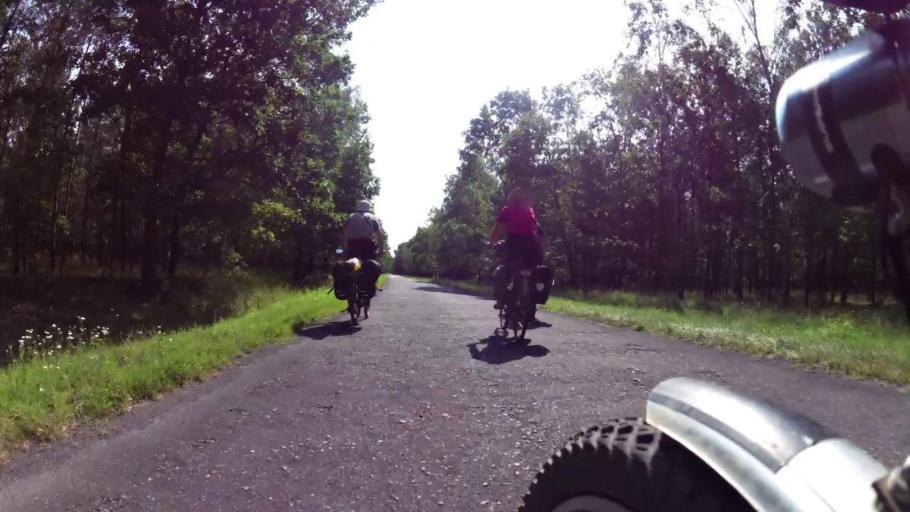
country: PL
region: West Pomeranian Voivodeship
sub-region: Powiat mysliborski
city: Boleszkowice
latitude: 52.6726
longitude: 14.5226
